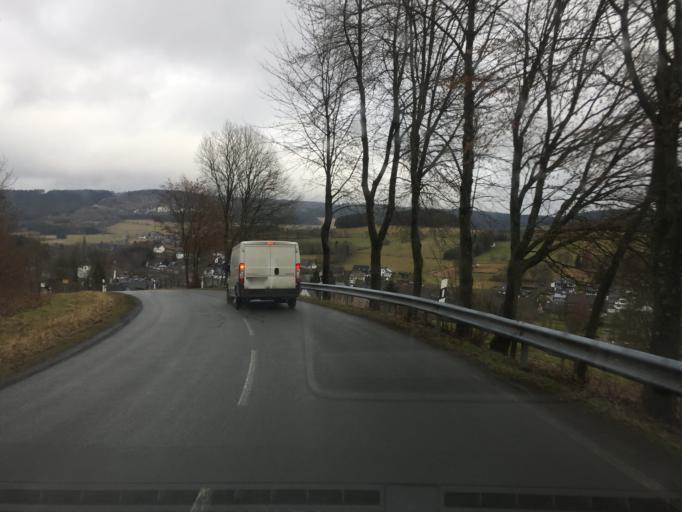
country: DE
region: North Rhine-Westphalia
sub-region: Regierungsbezirk Arnsberg
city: Winterberg
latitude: 51.2260
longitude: 8.5592
